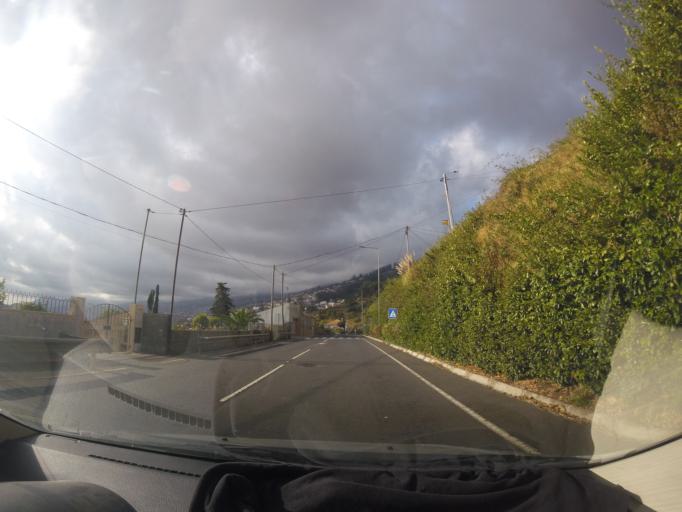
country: PT
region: Madeira
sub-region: Funchal
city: Nossa Senhora do Monte
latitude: 32.6540
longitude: -16.8775
